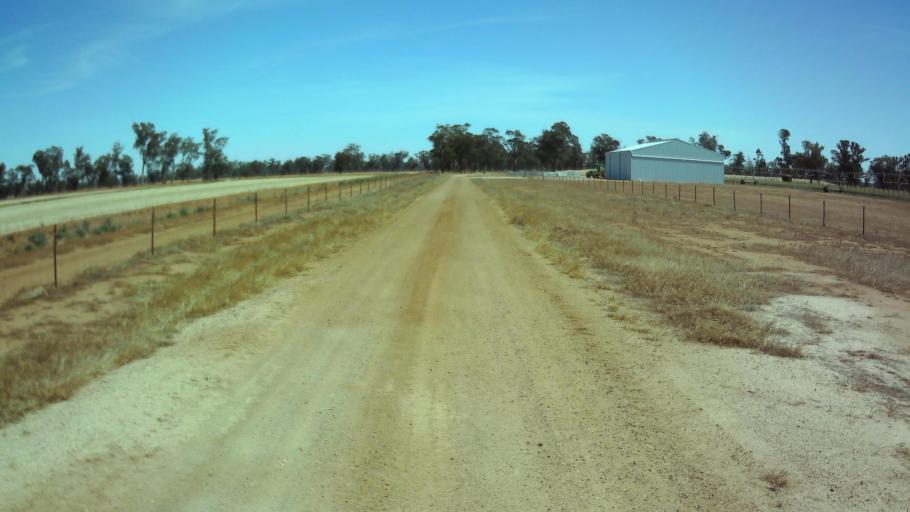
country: AU
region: New South Wales
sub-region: Weddin
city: Grenfell
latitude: -34.1170
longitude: 147.8156
